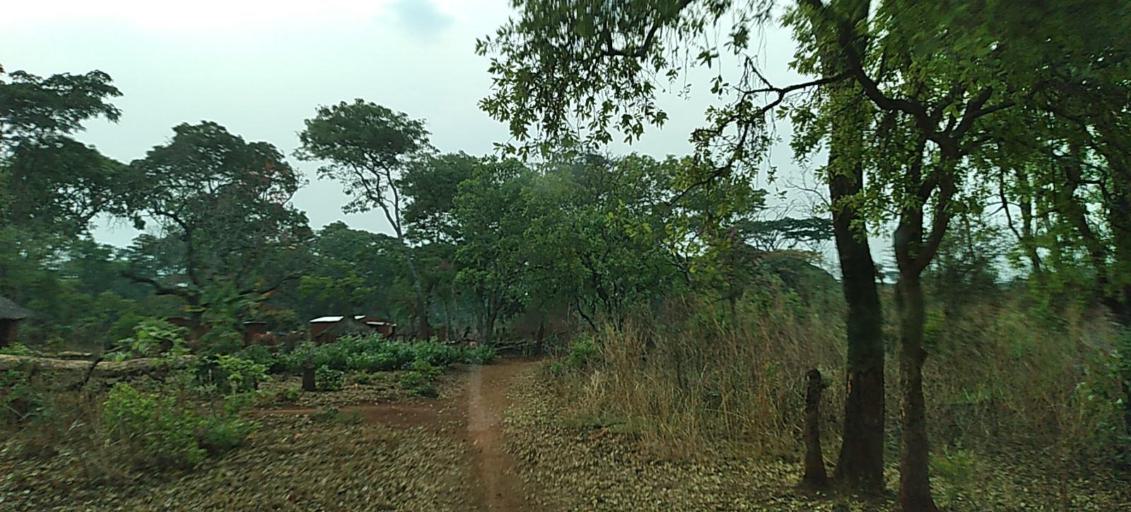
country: ZM
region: North-Western
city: Solwezi
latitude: -12.0450
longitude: 26.0078
